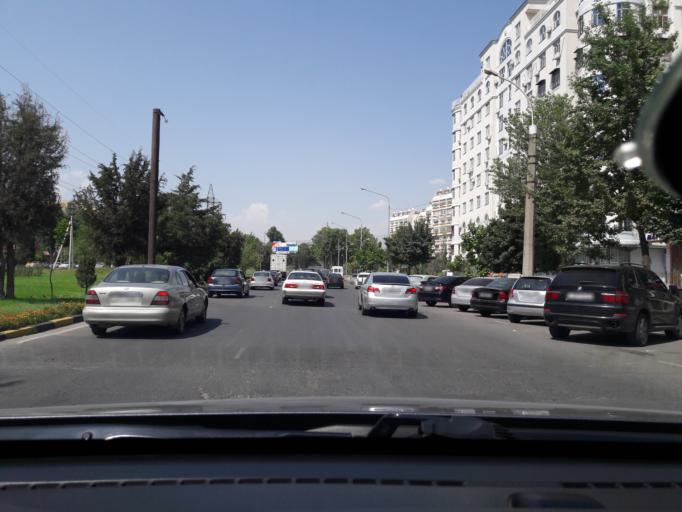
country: TJ
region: Dushanbe
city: Dushanbe
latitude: 38.5901
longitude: 68.7421
